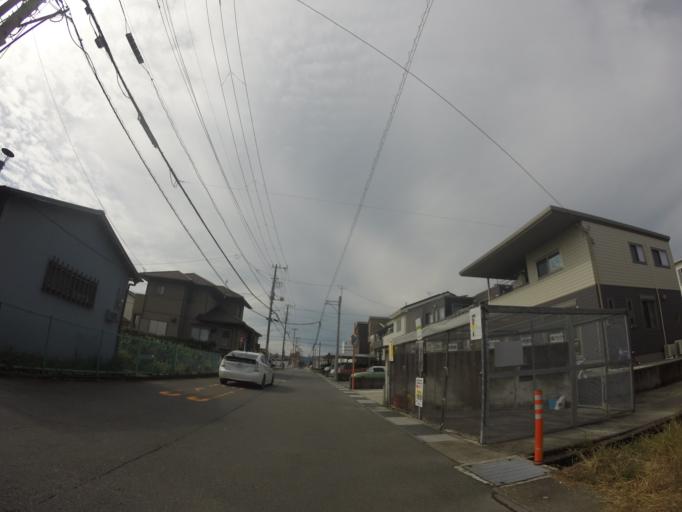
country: JP
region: Shizuoka
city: Fuji
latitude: 35.1358
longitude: 138.6517
